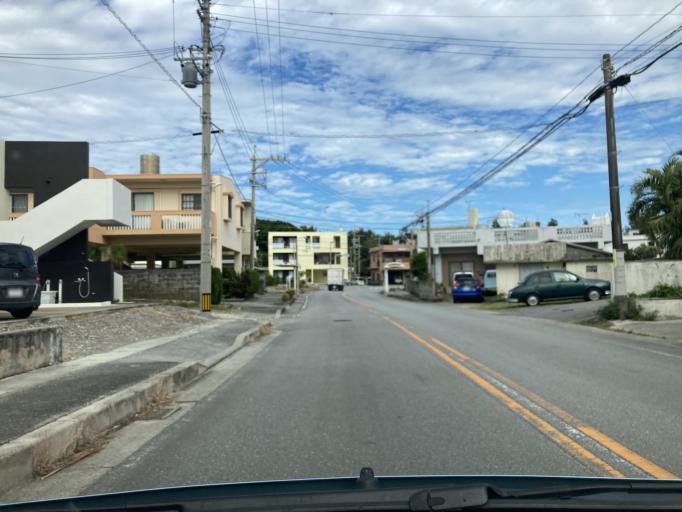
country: JP
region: Okinawa
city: Ishikawa
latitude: 26.4365
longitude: 127.7783
